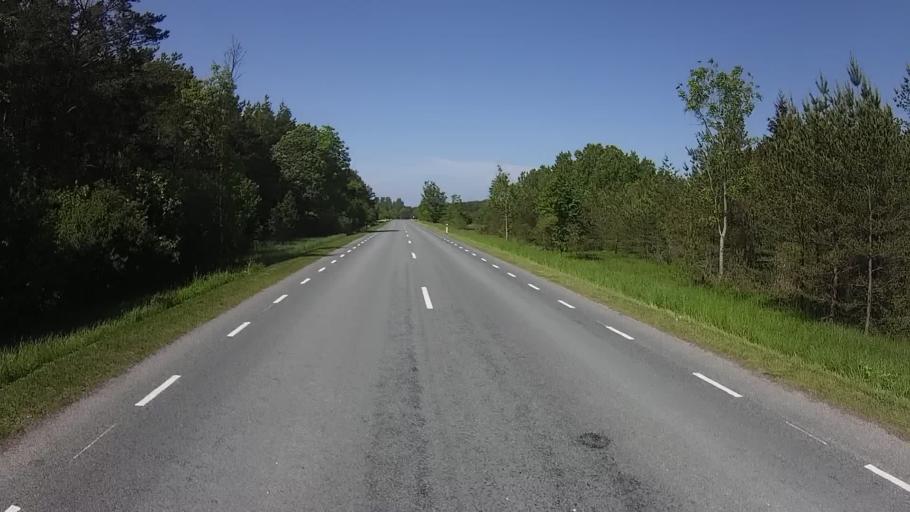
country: EE
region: Saare
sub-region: Kuressaare linn
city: Kuressaare
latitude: 58.3707
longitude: 22.4359
